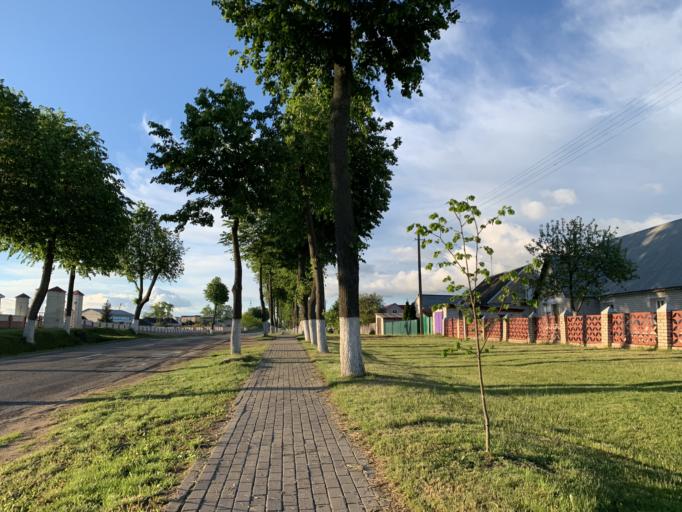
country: BY
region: Minsk
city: Nyasvizh
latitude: 53.2087
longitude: 26.6961
